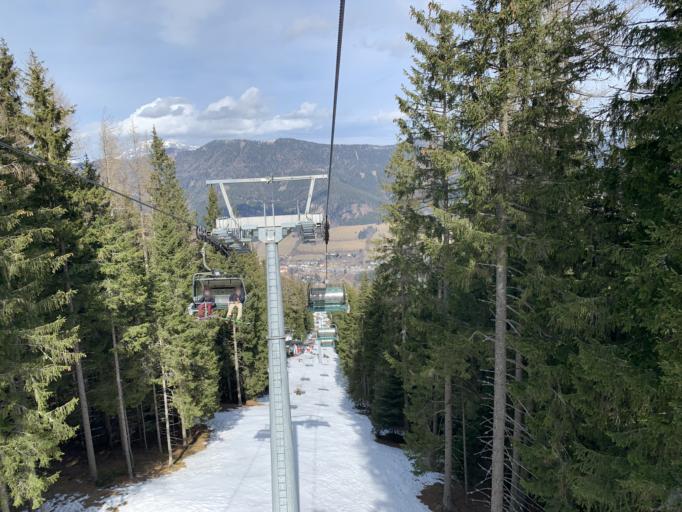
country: AT
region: Styria
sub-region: Politischer Bezirk Bruck-Muerzzuschlag
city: Spital am Semmering
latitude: 47.5933
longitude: 15.7637
